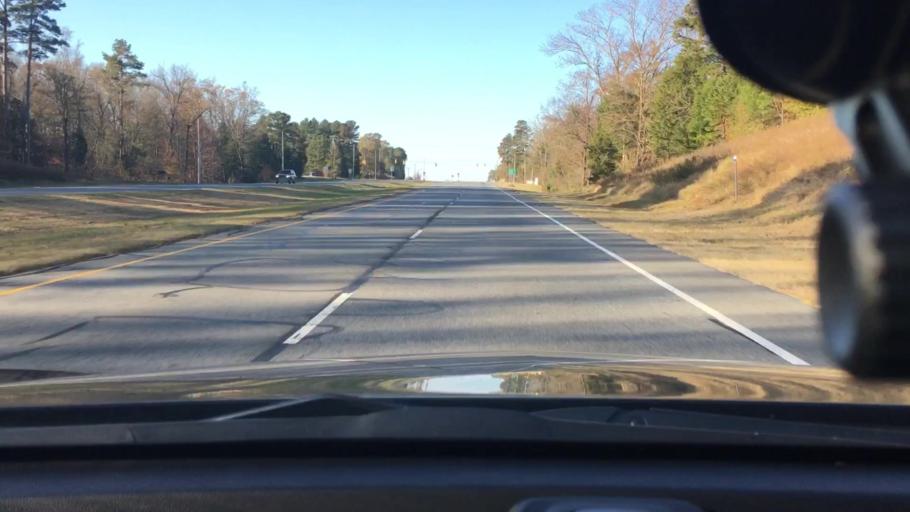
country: US
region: North Carolina
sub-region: Cabarrus County
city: Mount Pleasant
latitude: 35.3961
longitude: -80.4783
